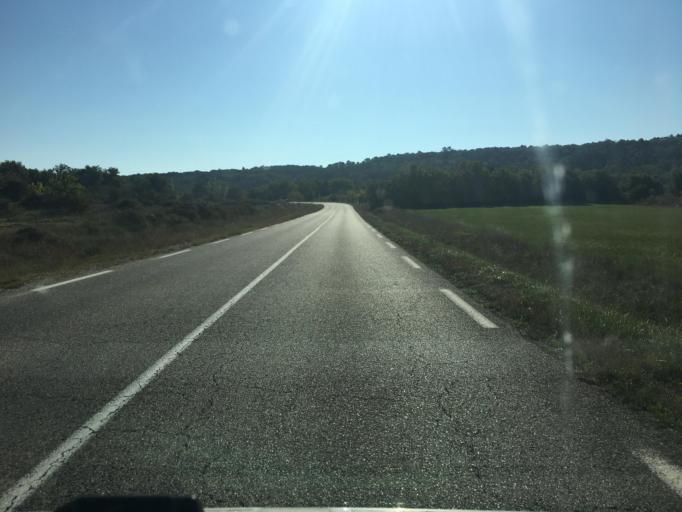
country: FR
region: Languedoc-Roussillon
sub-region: Departement du Gard
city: Saint-Quentin-la-Poterie
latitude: 44.1323
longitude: 4.4092
